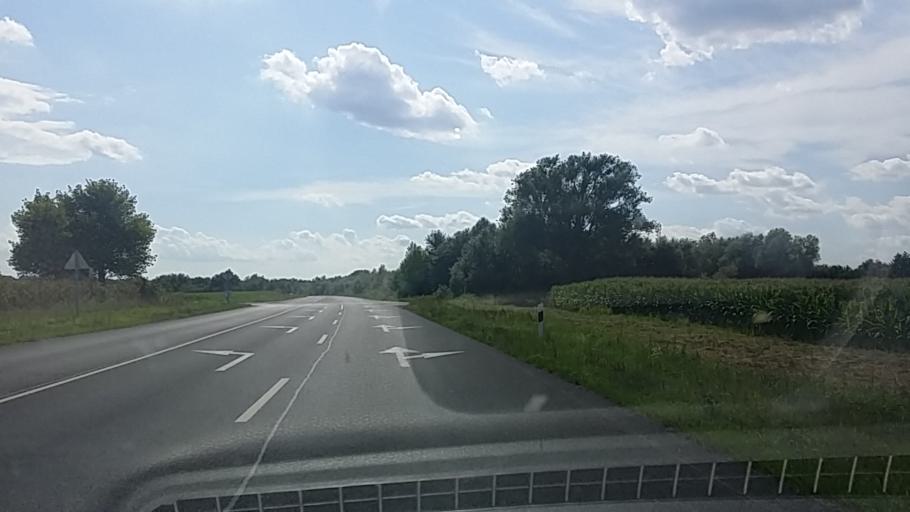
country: HU
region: Zala
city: Nagykanizsa
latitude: 46.4663
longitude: 16.9588
